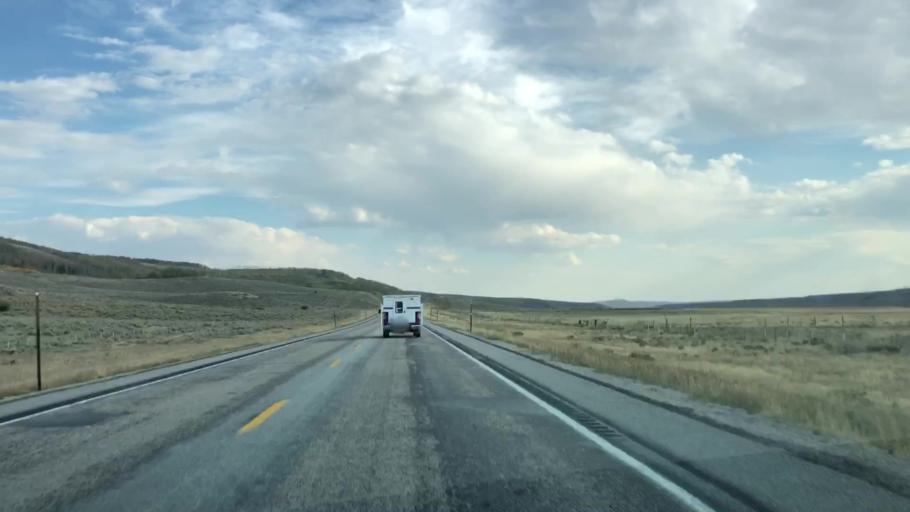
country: US
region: Wyoming
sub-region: Sublette County
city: Pinedale
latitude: 43.0988
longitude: -110.1684
